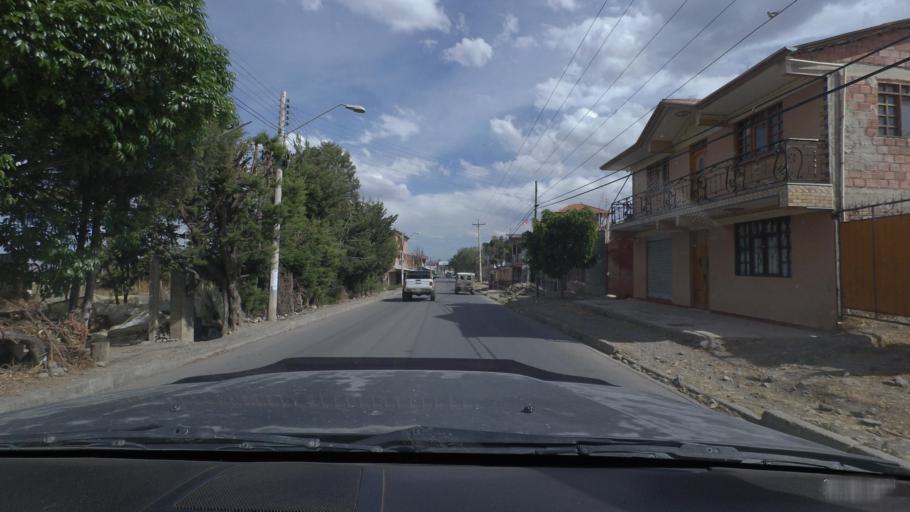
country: BO
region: Cochabamba
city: Cochabamba
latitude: -17.3281
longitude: -66.2825
